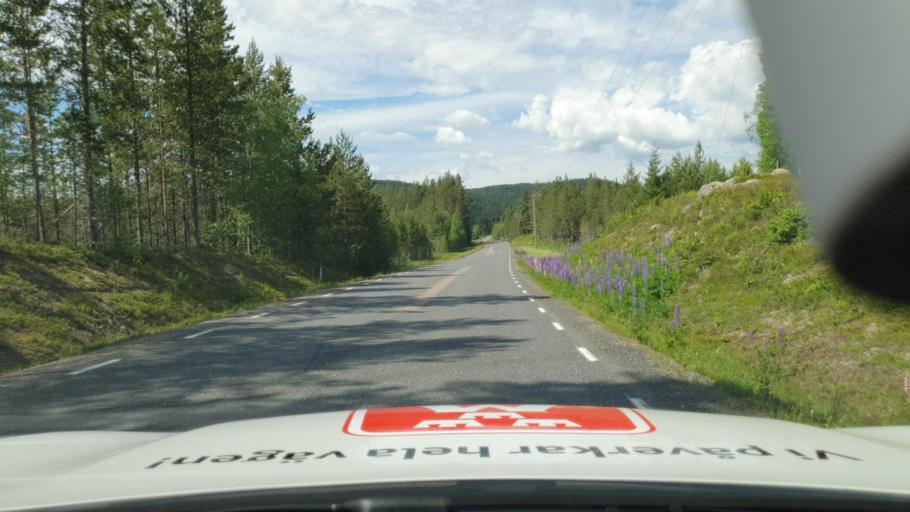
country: SE
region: Vaermland
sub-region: Torsby Kommun
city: Torsby
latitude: 60.5644
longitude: 12.7514
